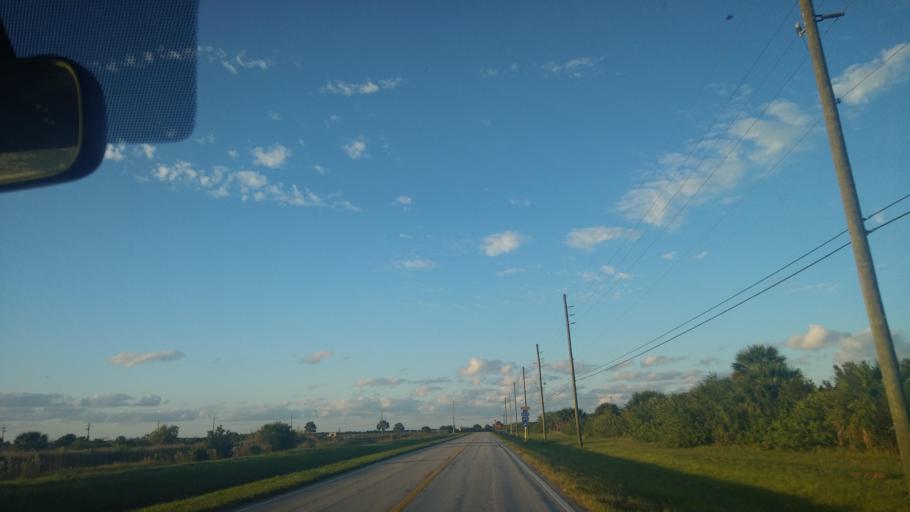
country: US
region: Florida
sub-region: Indian River County
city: Fellsmere
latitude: 27.7367
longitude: -80.6423
